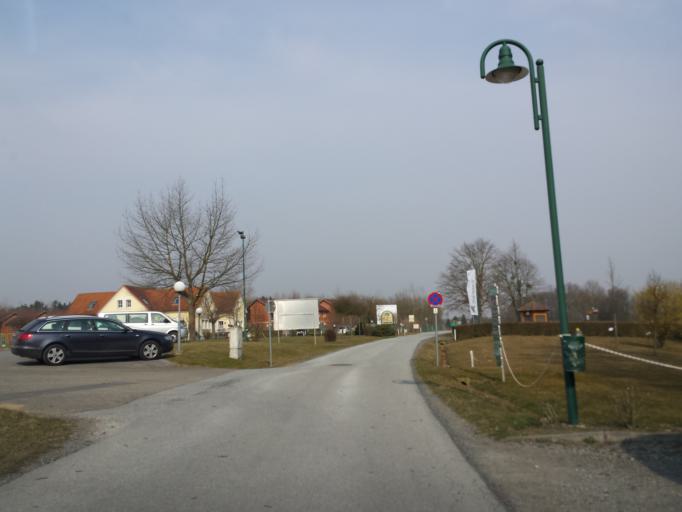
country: AT
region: Burgenland
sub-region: Politischer Bezirk Jennersdorf
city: Konigsdorf
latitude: 47.0039
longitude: 16.1366
